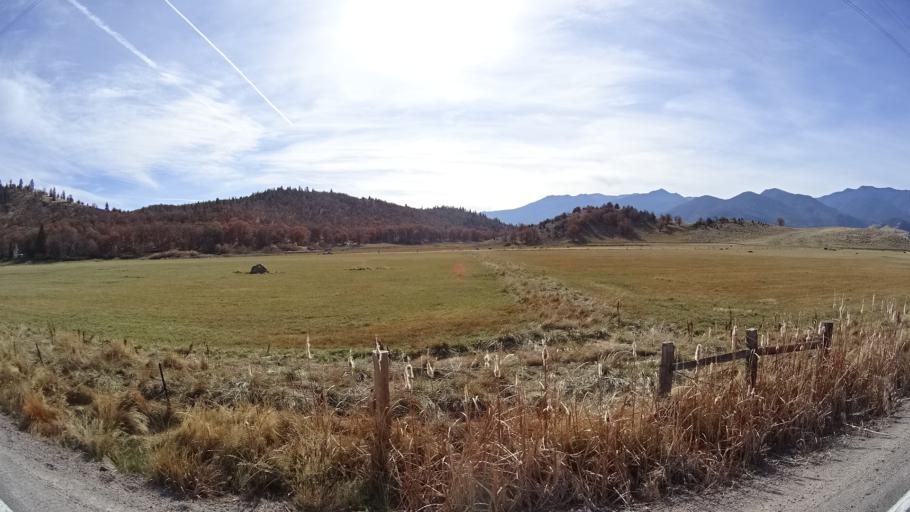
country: US
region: California
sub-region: Siskiyou County
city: Weed
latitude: 41.4677
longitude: -122.4181
